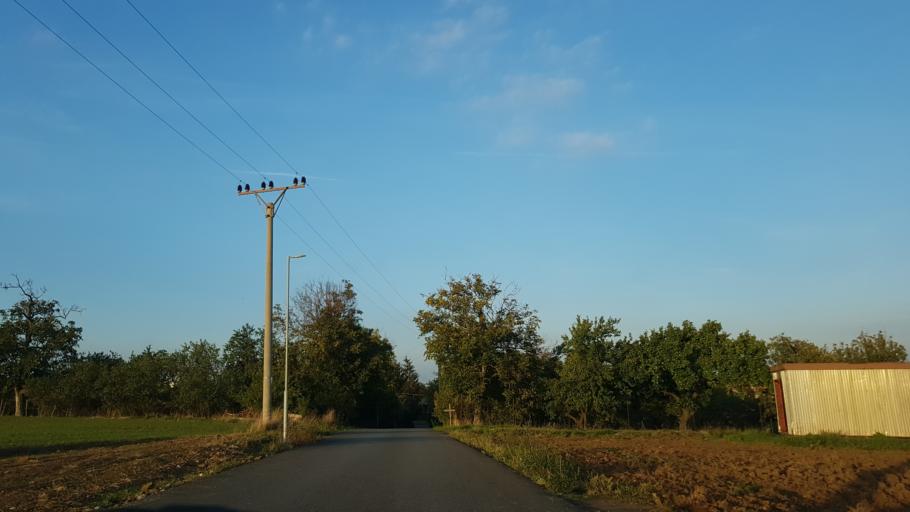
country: CZ
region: Zlin
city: Polesovice
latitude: 49.0264
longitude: 17.3503
